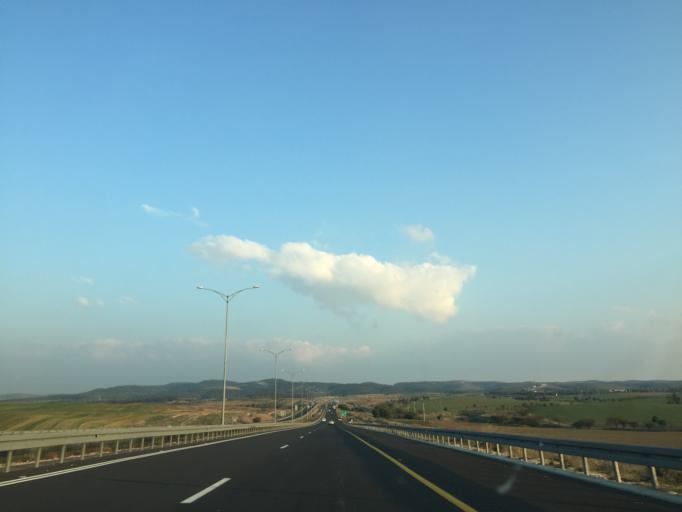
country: IL
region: Southern District
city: Lehavim
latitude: 31.3883
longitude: 34.8014
